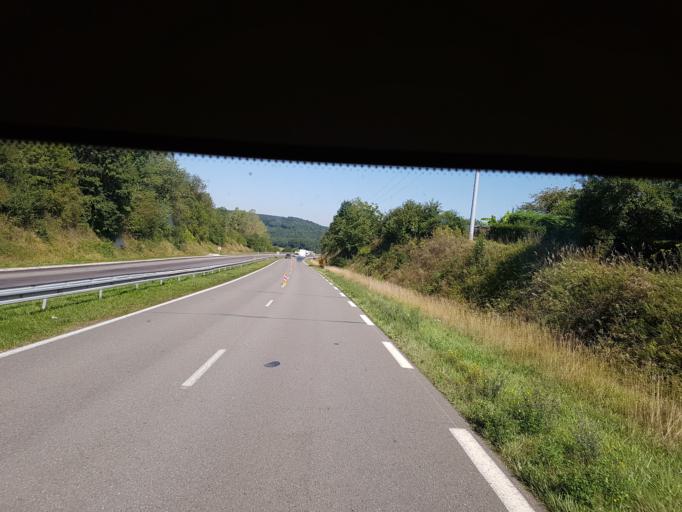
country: FR
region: Franche-Comte
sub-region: Departement du Jura
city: Montmorot
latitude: 46.7541
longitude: 5.5581
